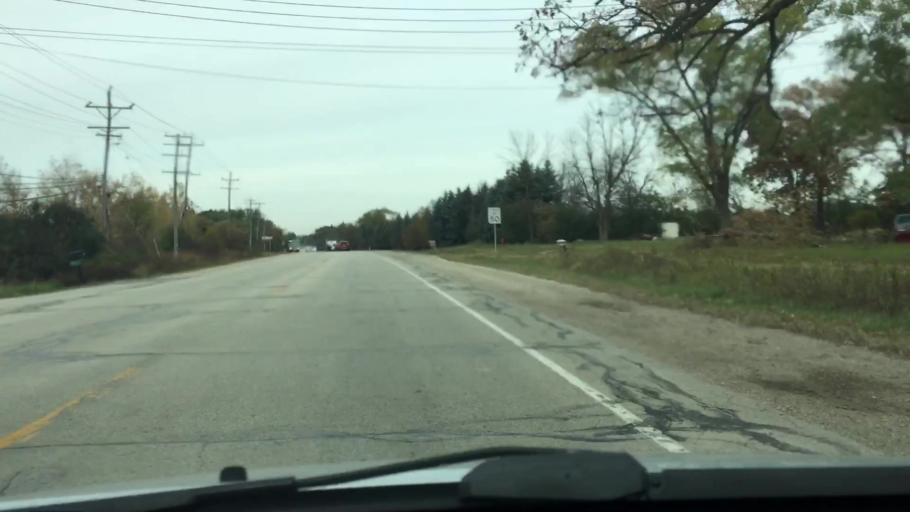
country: US
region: Wisconsin
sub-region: Milwaukee County
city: Franklin
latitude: 42.8809
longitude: -88.0298
